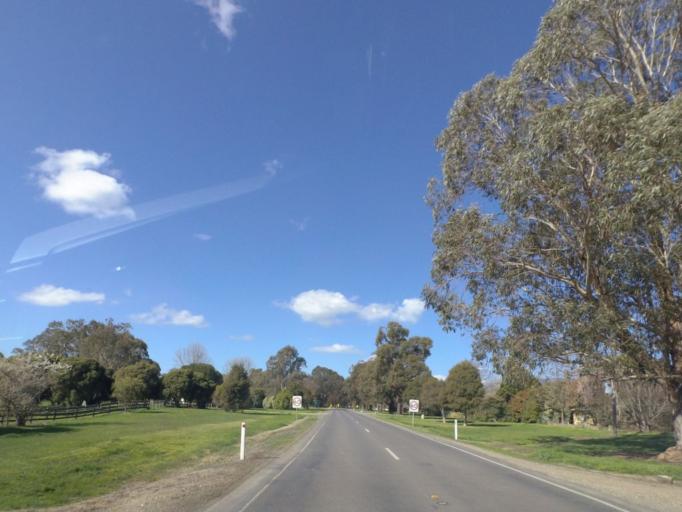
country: AU
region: Victoria
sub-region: Murrindindi
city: Alexandra
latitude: -37.2543
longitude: 145.7920
